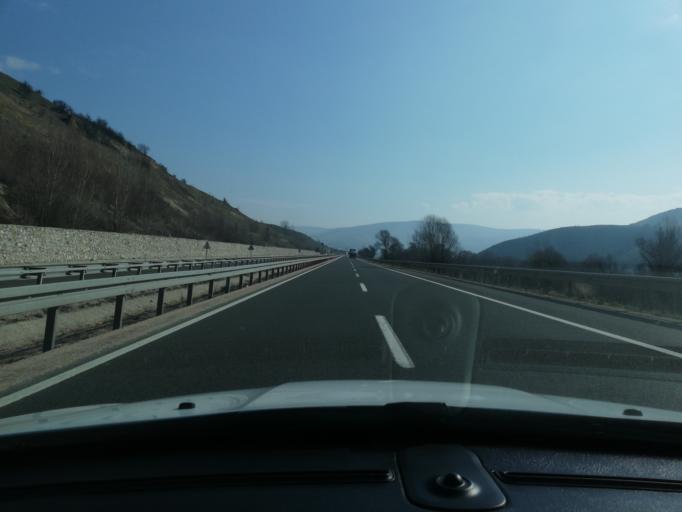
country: TR
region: Cankiri
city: Cerkes
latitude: 40.8331
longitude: 32.7367
